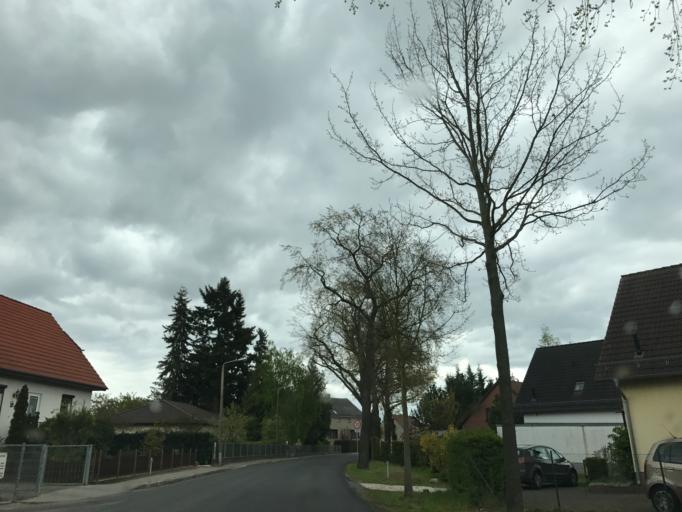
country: DE
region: Brandenburg
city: Dallgow-Doeberitz
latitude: 52.4706
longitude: 13.0094
